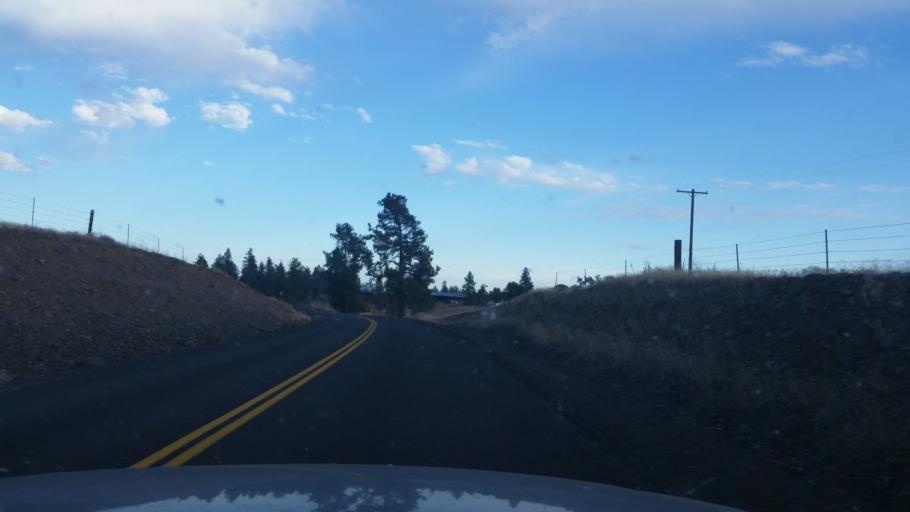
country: US
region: Washington
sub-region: Spokane County
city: Medical Lake
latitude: 47.4518
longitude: -117.7998
